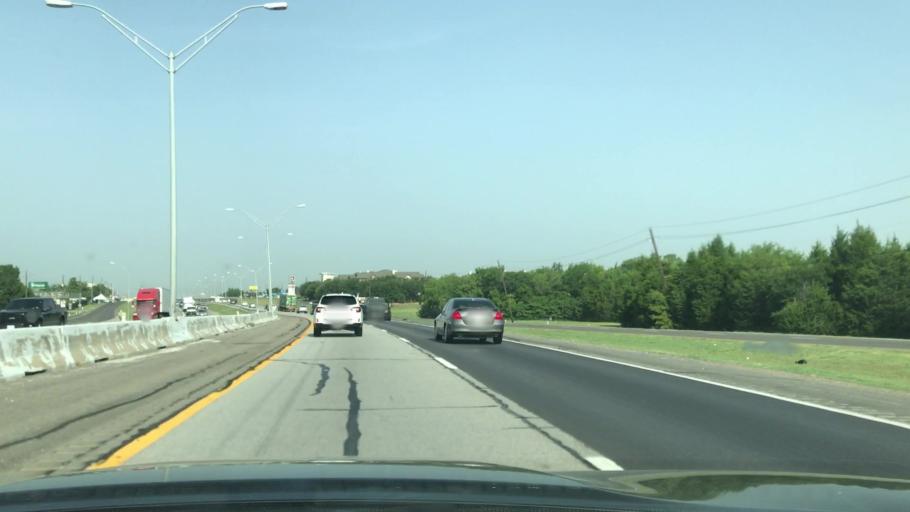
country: US
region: Texas
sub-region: Dallas County
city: Mesquite
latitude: 32.7924
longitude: -96.6054
